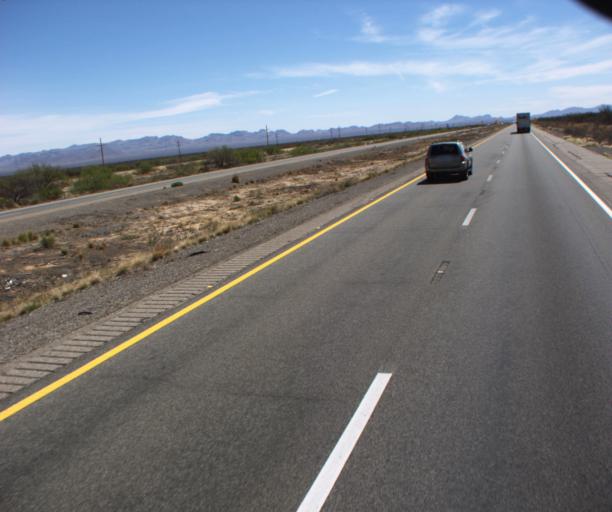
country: US
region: Arizona
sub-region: Cochise County
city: Willcox
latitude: 32.2891
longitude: -109.3186
